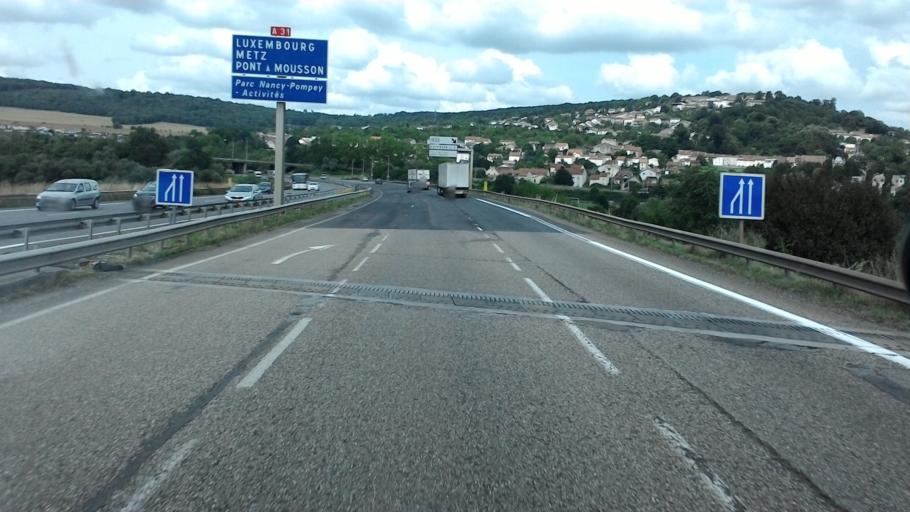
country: FR
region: Lorraine
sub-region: Departement de Meurthe-et-Moselle
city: Bouxieres-aux-Dames
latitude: 48.7475
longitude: 6.1554
